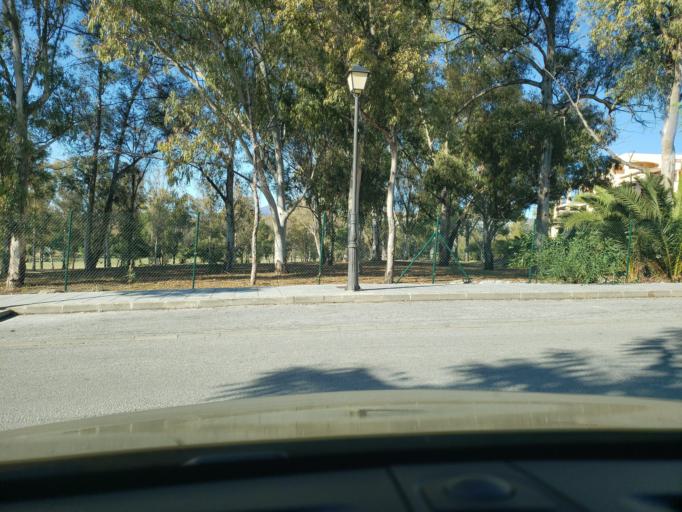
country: ES
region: Andalusia
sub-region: Provincia de Malaga
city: Benahavis
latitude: 36.4865
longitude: -5.0176
